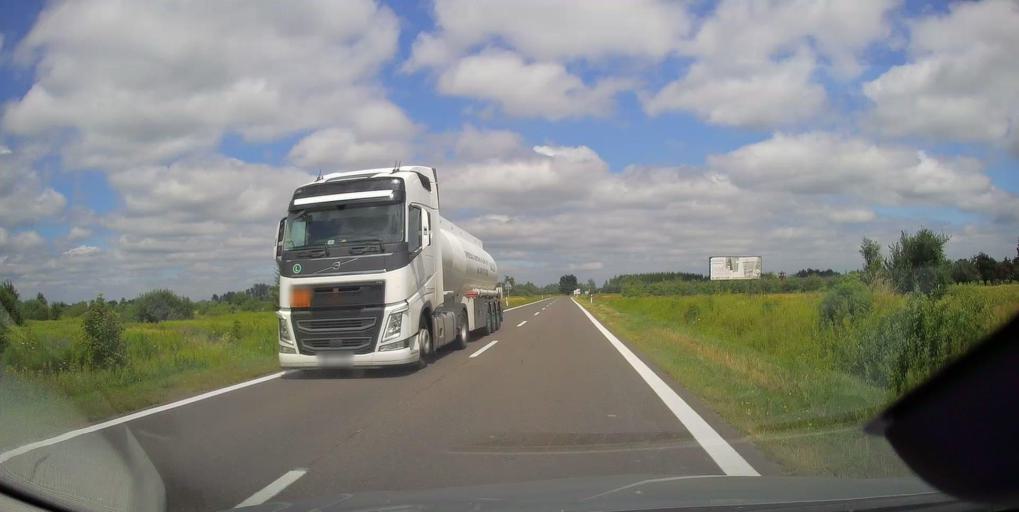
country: PL
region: Subcarpathian Voivodeship
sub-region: Powiat tarnobrzeski
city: Baranow Sandomierski
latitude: 50.4985
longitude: 21.5707
